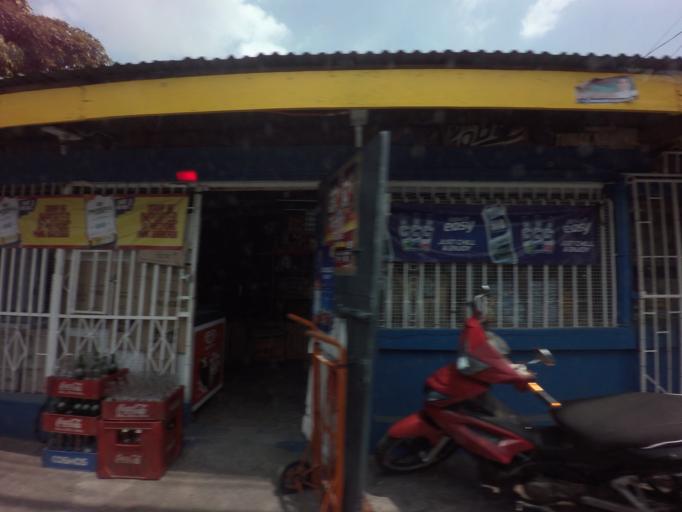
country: PH
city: Sambayanihan People's Village
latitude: 14.4647
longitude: 121.0555
